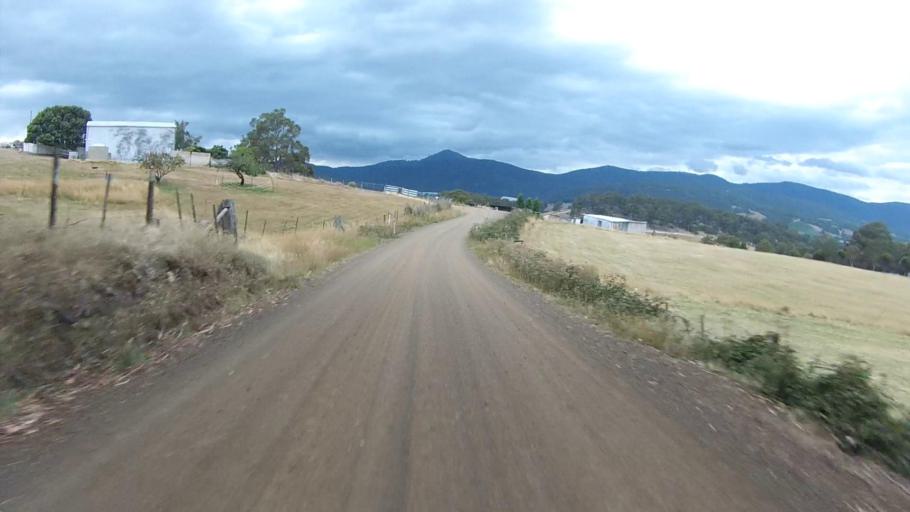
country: AU
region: Tasmania
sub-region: Huon Valley
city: Huonville
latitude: -42.9705
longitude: 147.0625
